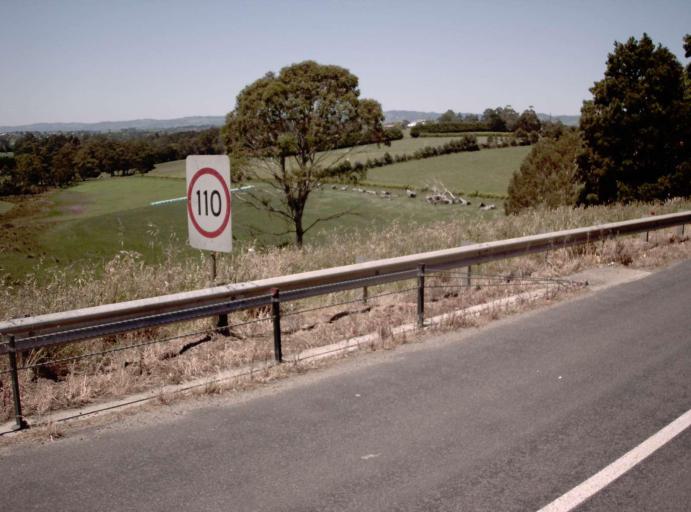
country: AU
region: Victoria
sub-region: Baw Baw
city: Warragul
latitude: -38.1438
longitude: 145.8847
